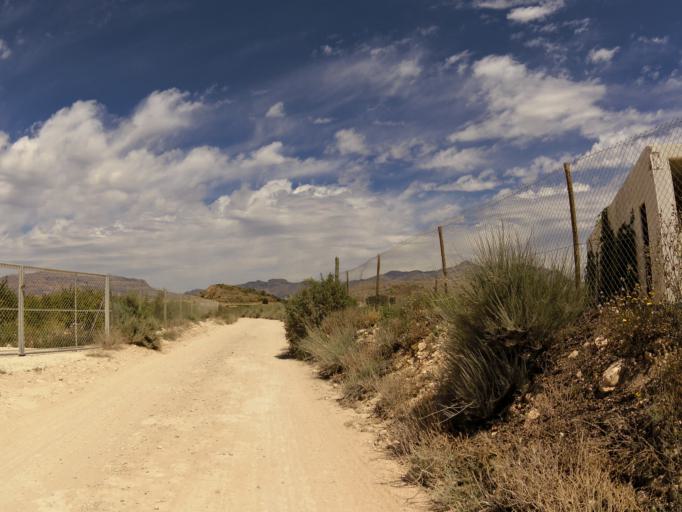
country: ES
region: Valencia
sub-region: Provincia de Alicante
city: Agost
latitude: 38.4037
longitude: -0.6107
